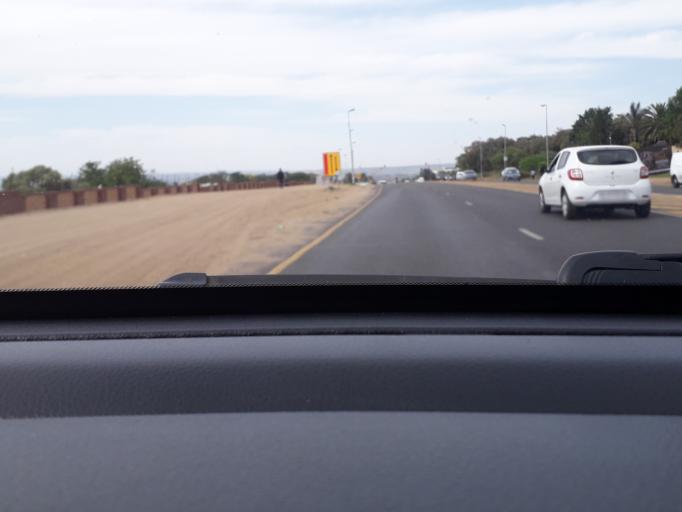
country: ZA
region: Gauteng
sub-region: West Rand District Municipality
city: Muldersdriseloop
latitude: -26.0565
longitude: 27.9456
